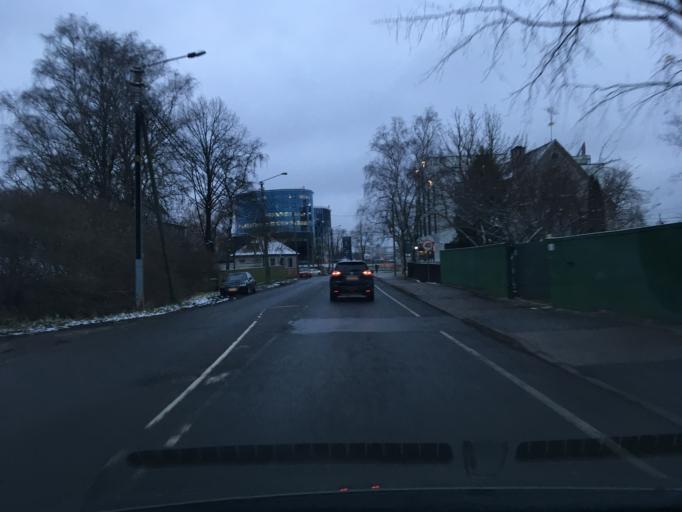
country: EE
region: Harju
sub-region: Tallinna linn
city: Tallinn
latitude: 59.4156
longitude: 24.7544
